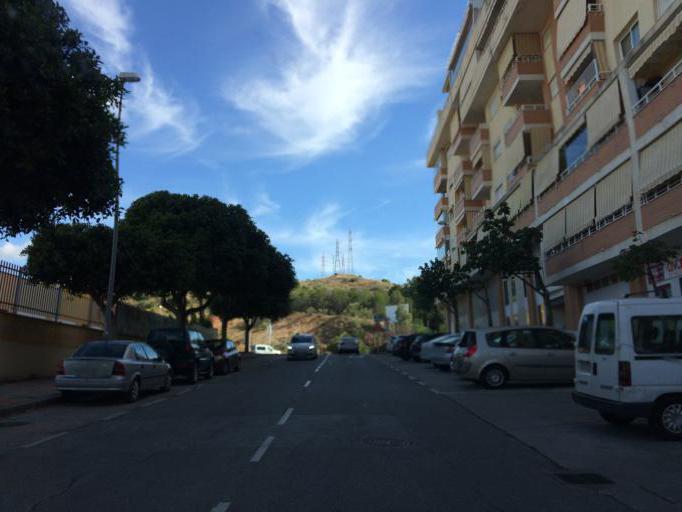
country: ES
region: Andalusia
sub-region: Provincia de Malaga
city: Malaga
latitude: 36.7258
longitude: -4.4799
